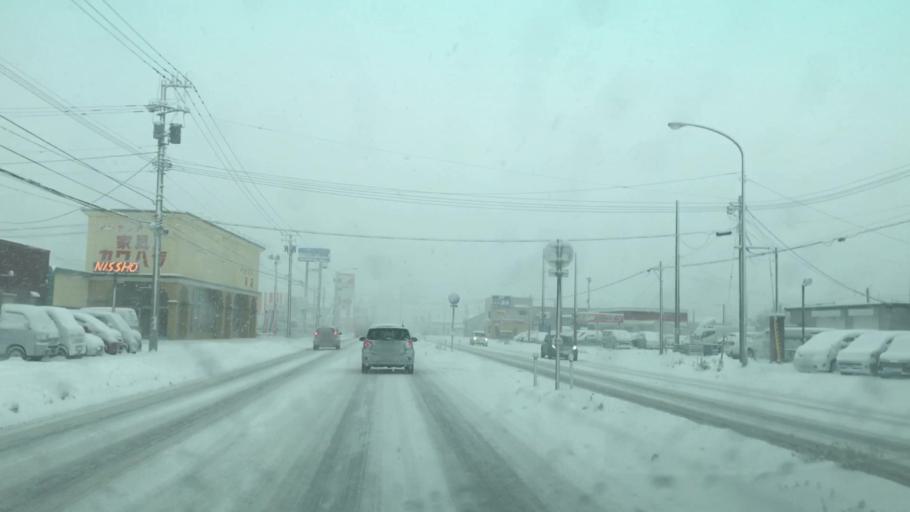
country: JP
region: Hokkaido
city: Muroran
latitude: 42.3840
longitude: 141.0765
